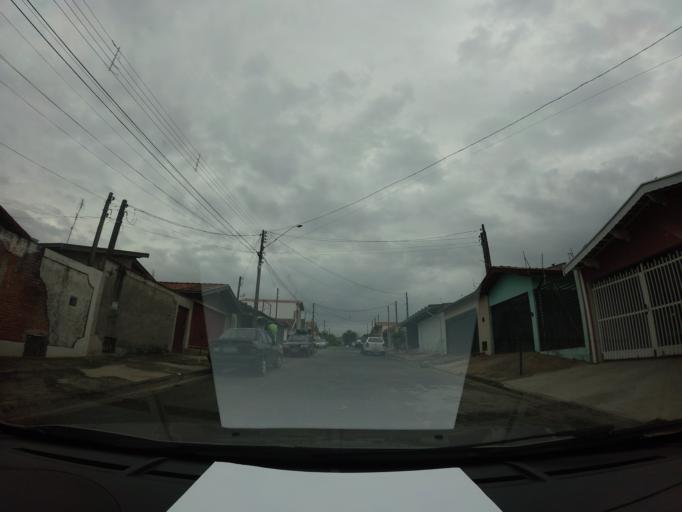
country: BR
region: Sao Paulo
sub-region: Piracicaba
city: Piracicaba
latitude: -22.7578
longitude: -47.5993
